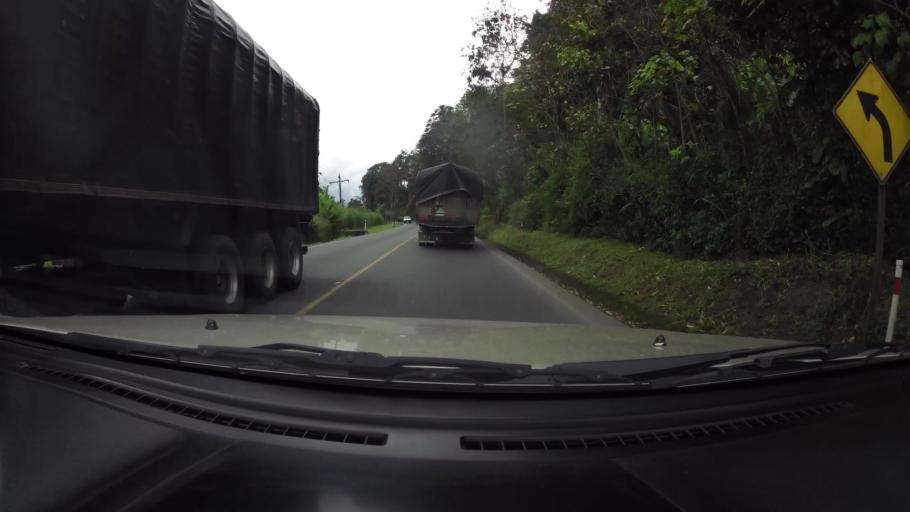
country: EC
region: Santo Domingo de los Tsachilas
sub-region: Canton Santo Domingo de los Colorados
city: Santo Domingo de los Colorados
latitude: -0.2774
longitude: -79.0762
